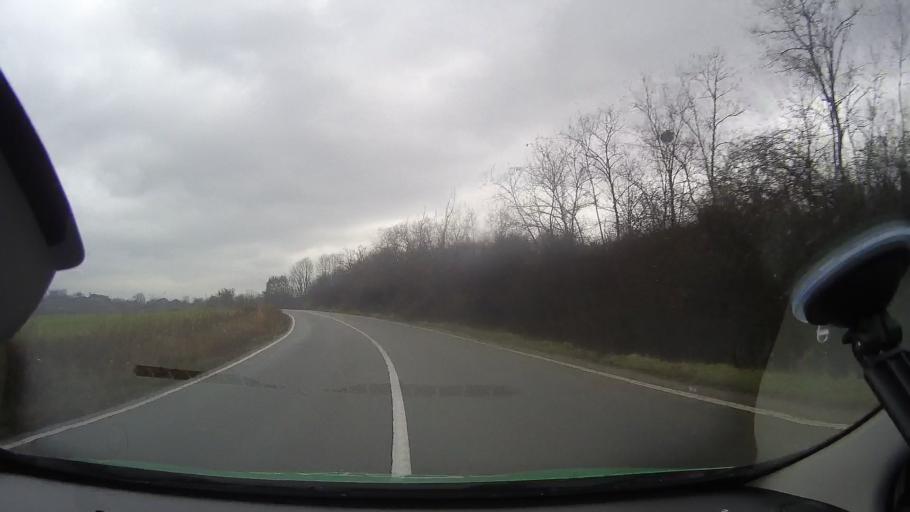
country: RO
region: Arad
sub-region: Comuna Almas
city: Almas
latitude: 46.2915
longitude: 22.2173
